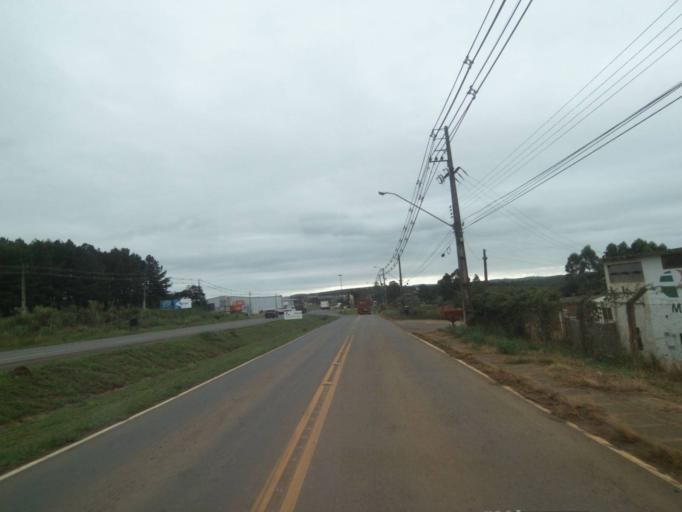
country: BR
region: Parana
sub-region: Telemaco Borba
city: Telemaco Borba
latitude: -24.3791
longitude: -50.6692
